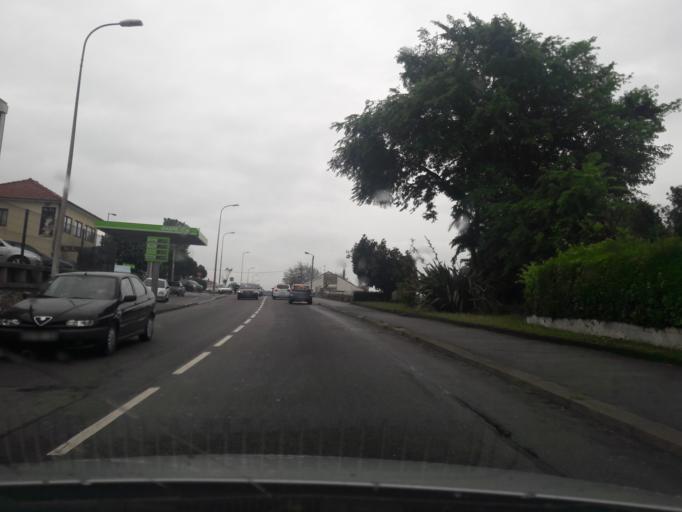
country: PT
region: Porto
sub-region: Vila do Conde
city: Vila do Conde
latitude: 41.3460
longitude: -8.7377
